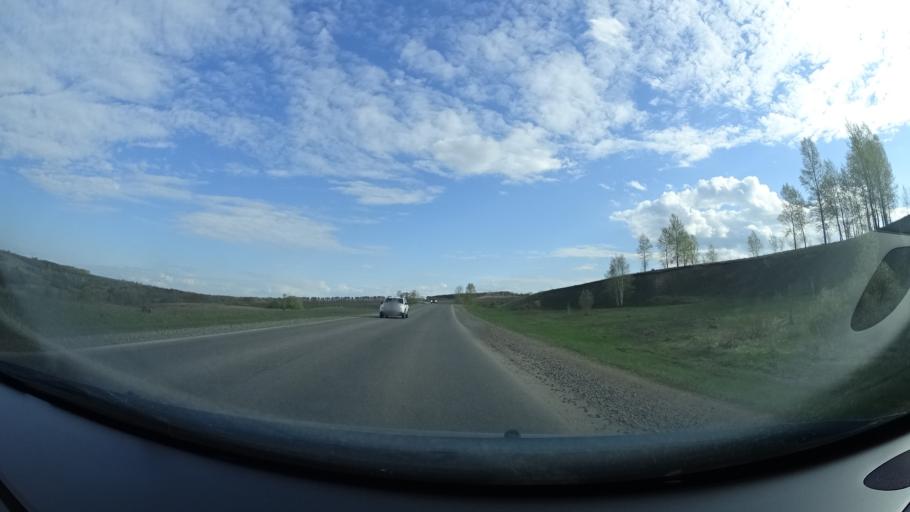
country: RU
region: Bashkortostan
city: Blagoveshchensk
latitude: 55.1198
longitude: 55.8410
